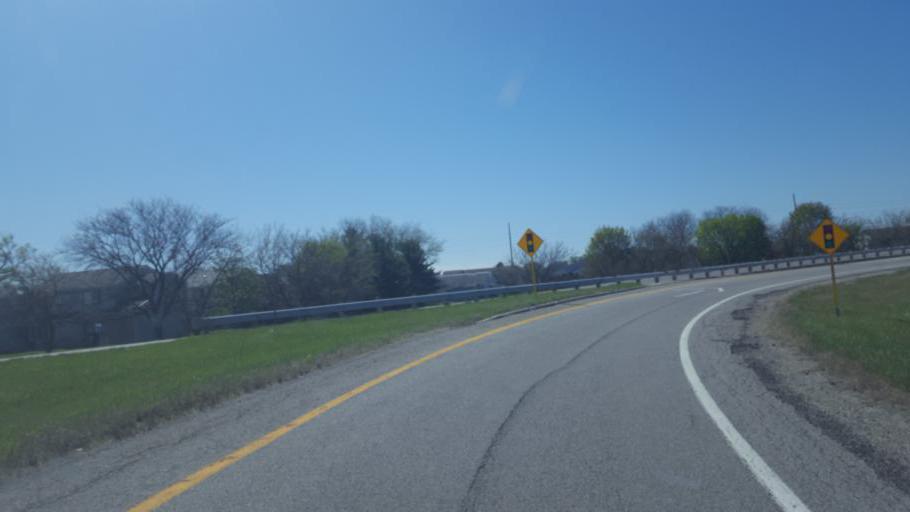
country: US
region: Ohio
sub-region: Sandusky County
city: Fremont
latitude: 41.3675
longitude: -83.1331
